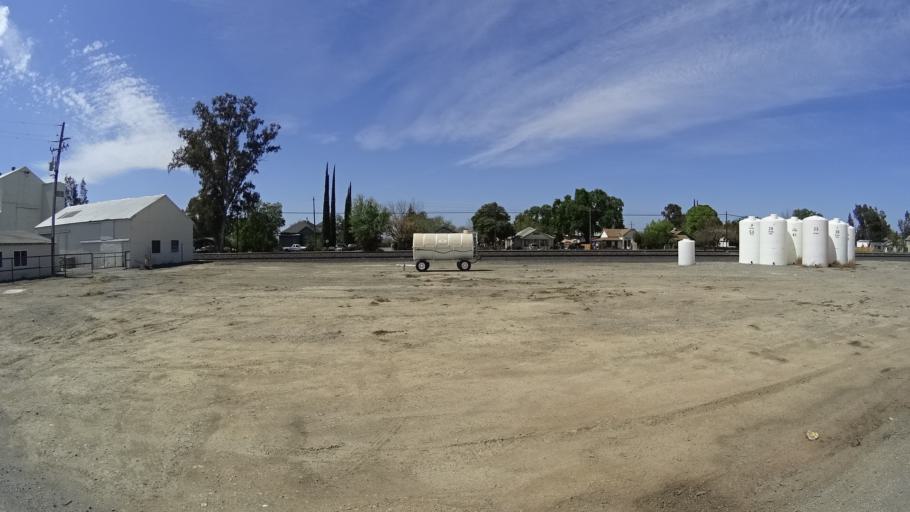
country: US
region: California
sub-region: Glenn County
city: Willows
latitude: 39.6167
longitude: -122.1930
